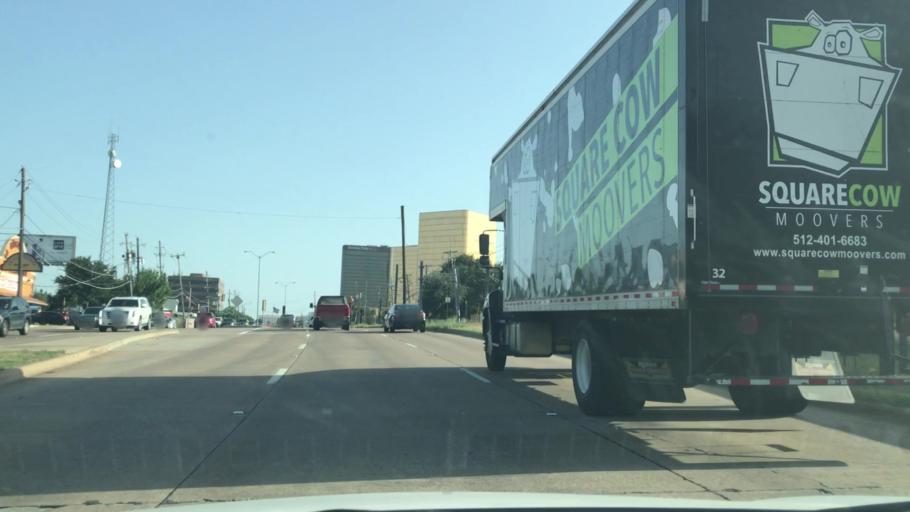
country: US
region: Texas
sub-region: Dallas County
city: University Park
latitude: 32.8684
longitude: -96.7667
